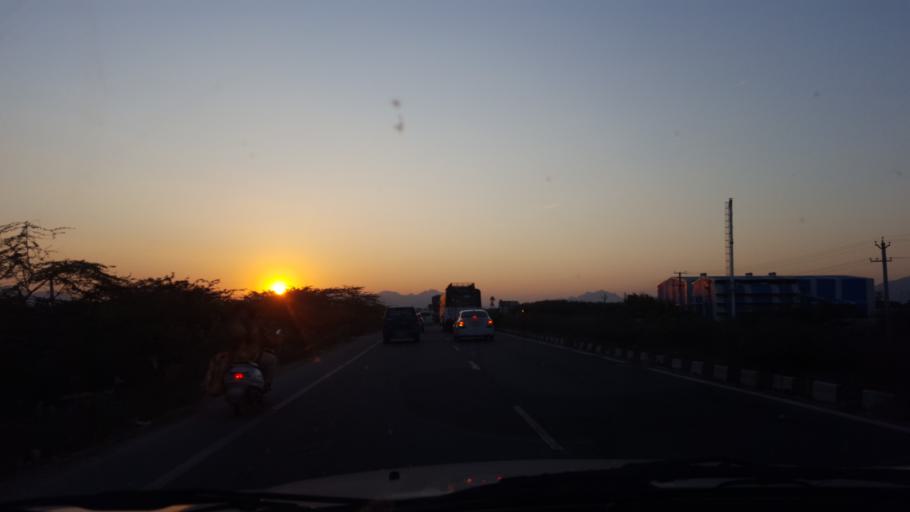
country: IN
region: Andhra Pradesh
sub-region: Chittoor
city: Tirupati
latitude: 13.6043
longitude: 79.3873
